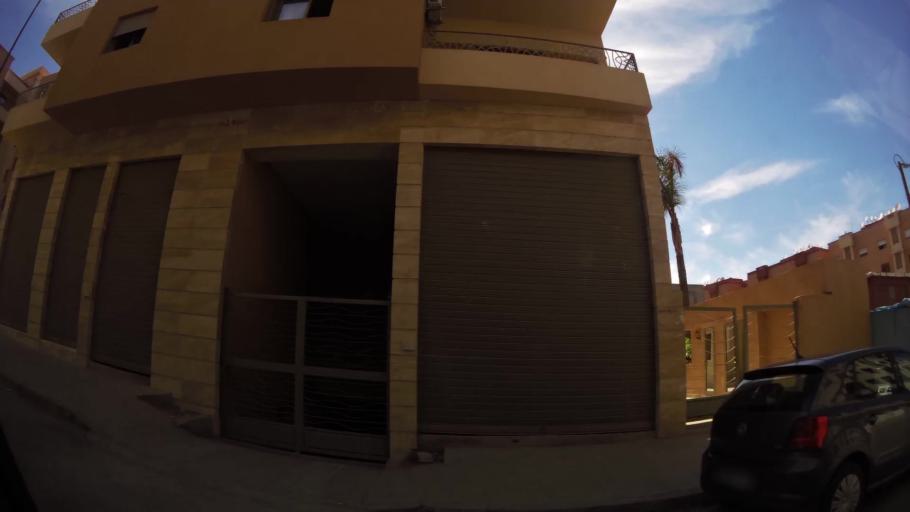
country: MA
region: Marrakech-Tensift-Al Haouz
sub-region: Marrakech
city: Marrakesh
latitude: 31.6591
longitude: -8.0204
